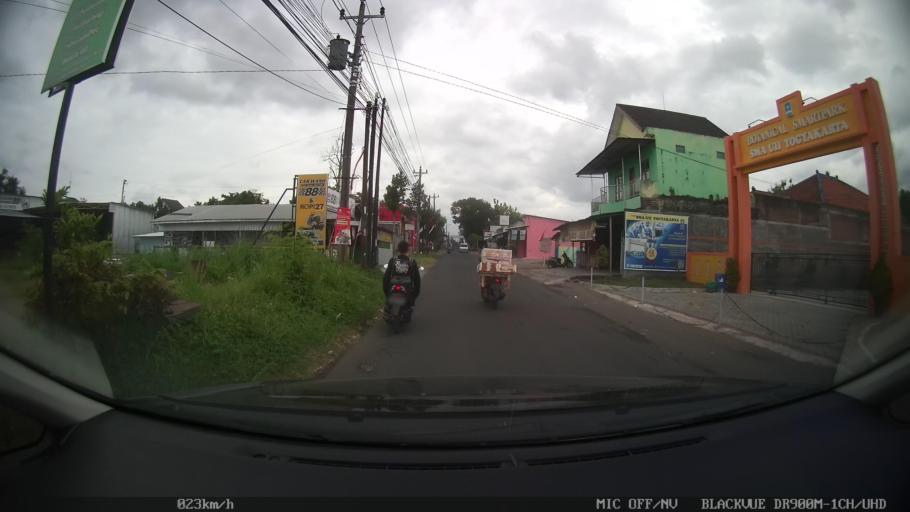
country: ID
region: Daerah Istimewa Yogyakarta
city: Sewon
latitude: -7.8370
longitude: 110.4118
